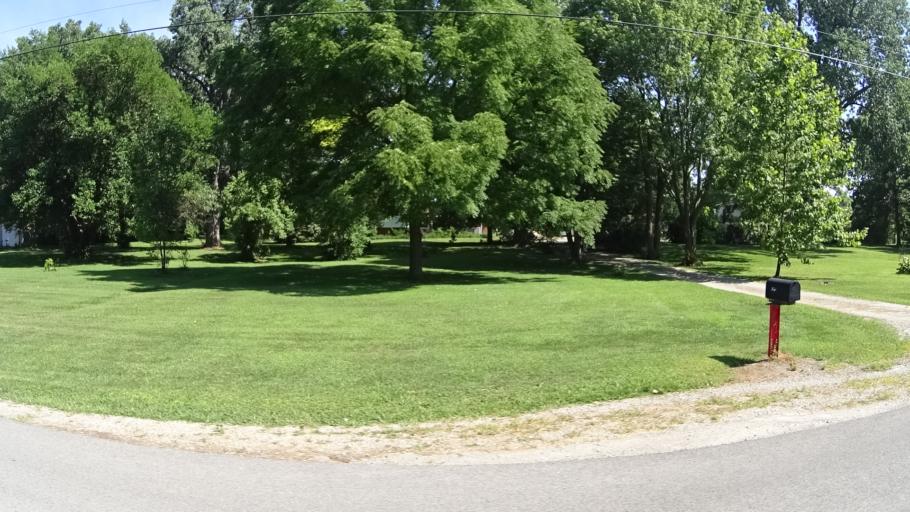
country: US
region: Ohio
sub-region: Ottawa County
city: Port Clinton
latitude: 41.4174
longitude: -82.8444
